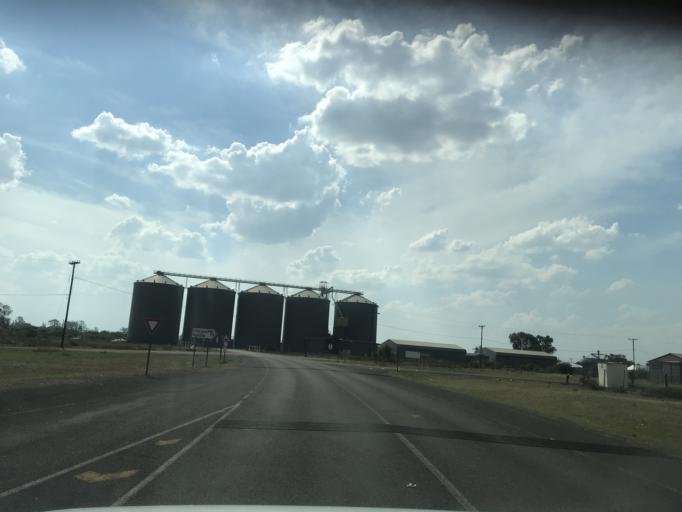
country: BW
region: South East
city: Janeng
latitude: -25.4742
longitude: 25.6028
